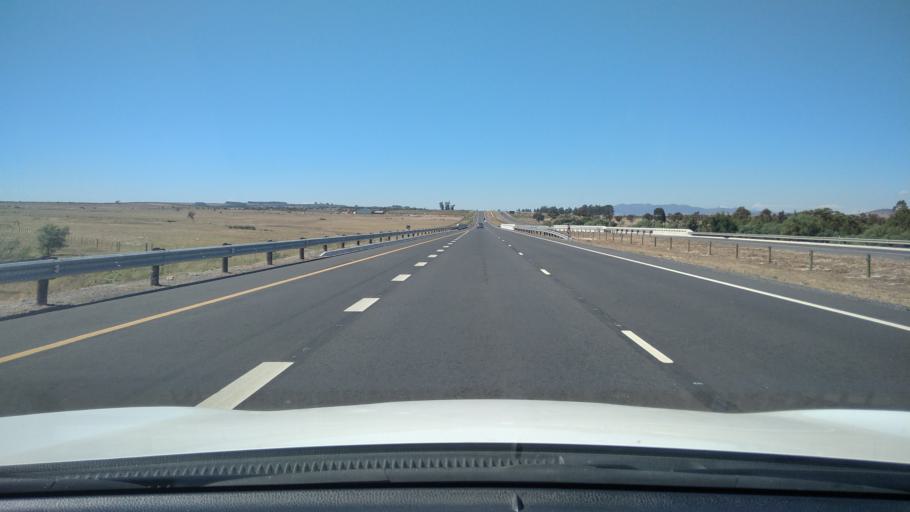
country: ZA
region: Western Cape
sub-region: City of Cape Town
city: Atlantis
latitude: -33.5752
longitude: 18.6167
